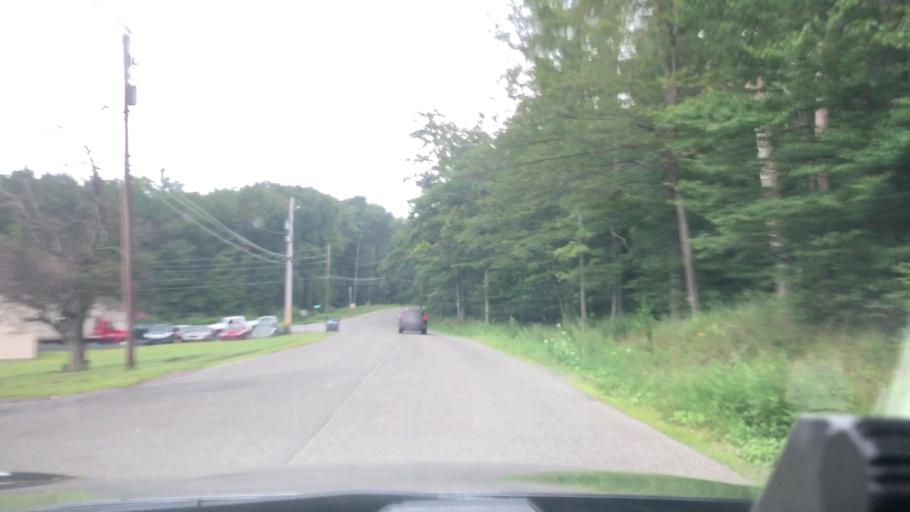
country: US
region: Pennsylvania
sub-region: Lackawanna County
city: Moscow
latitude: 41.2437
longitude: -75.4811
